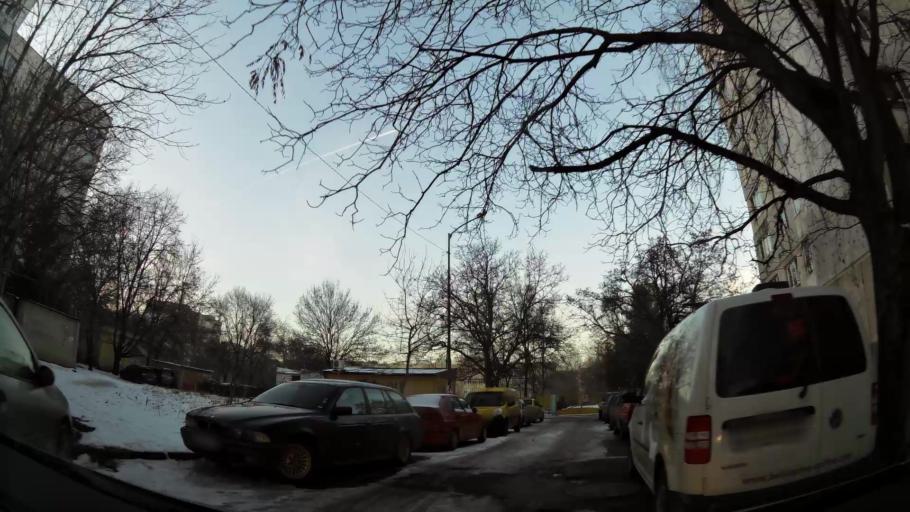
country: BG
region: Sofia-Capital
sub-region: Stolichna Obshtina
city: Sofia
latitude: 42.6844
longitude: 23.3729
